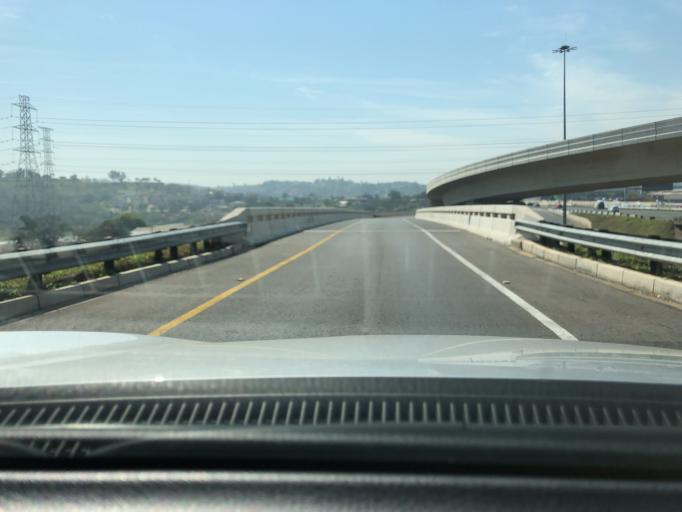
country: ZA
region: KwaZulu-Natal
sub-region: eThekwini Metropolitan Municipality
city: Berea
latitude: -29.8064
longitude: 30.9772
